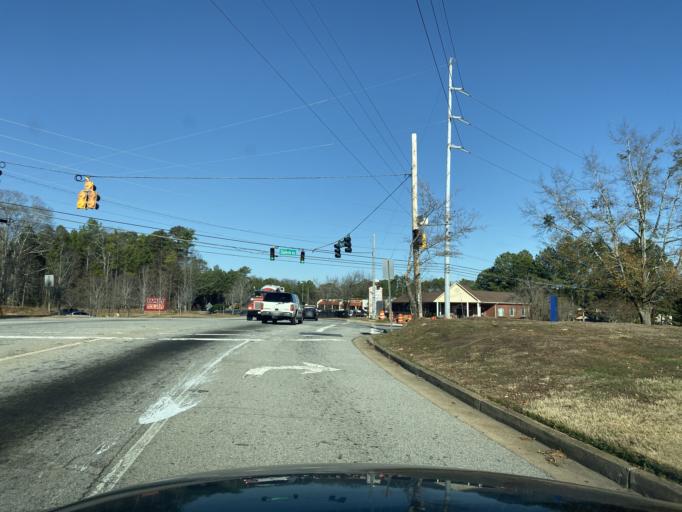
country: US
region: Georgia
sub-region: DeKalb County
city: Pine Mountain
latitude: 33.6783
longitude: -84.1786
